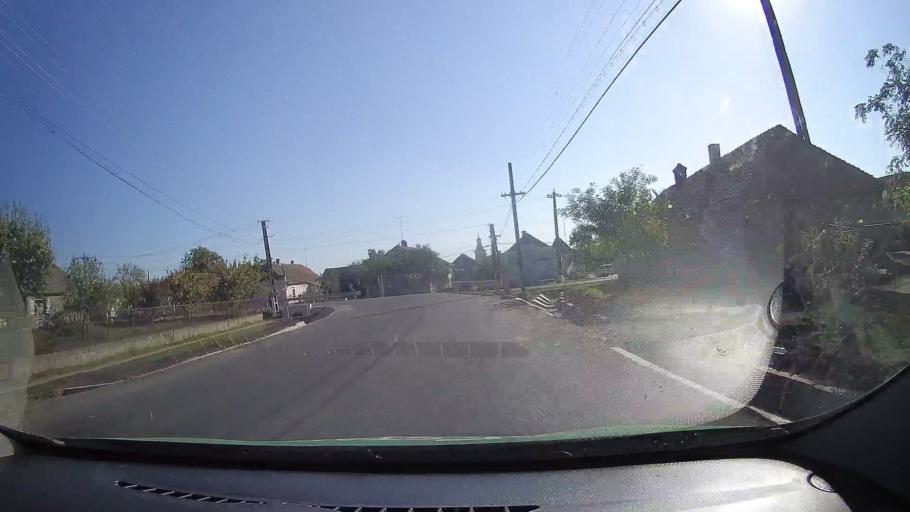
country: RO
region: Satu Mare
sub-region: Comuna Tiream
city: Tiream
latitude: 47.6137
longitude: 22.4710
